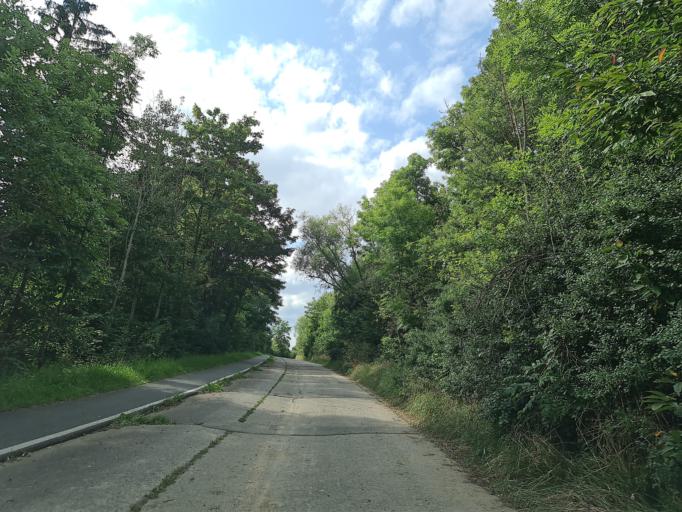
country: DE
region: Saxony
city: Syrau
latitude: 50.5008
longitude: 12.0734
